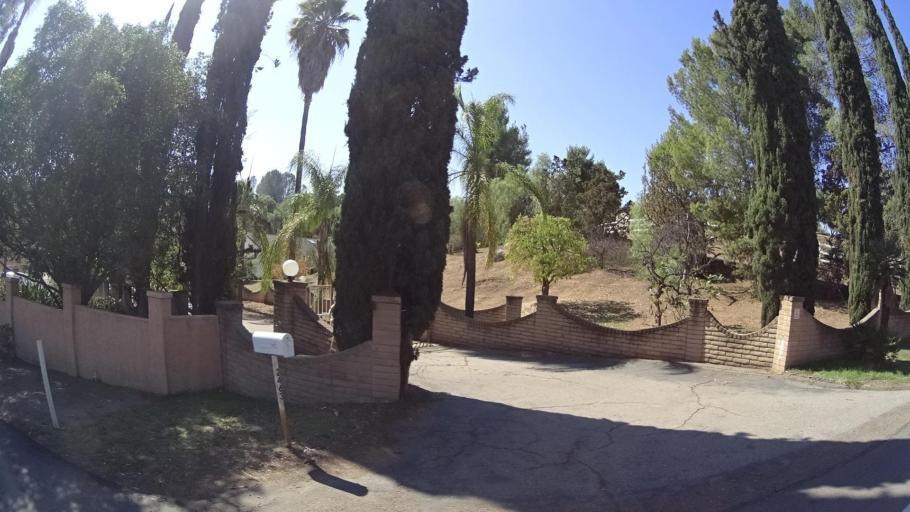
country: US
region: California
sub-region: San Diego County
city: Granite Hills
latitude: 32.7869
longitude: -116.8955
